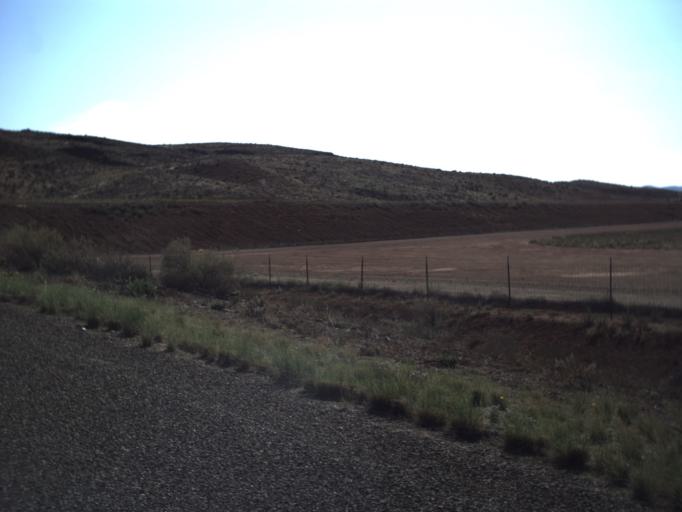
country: US
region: Utah
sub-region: Washington County
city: Saint George
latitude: 37.0225
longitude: -113.6022
